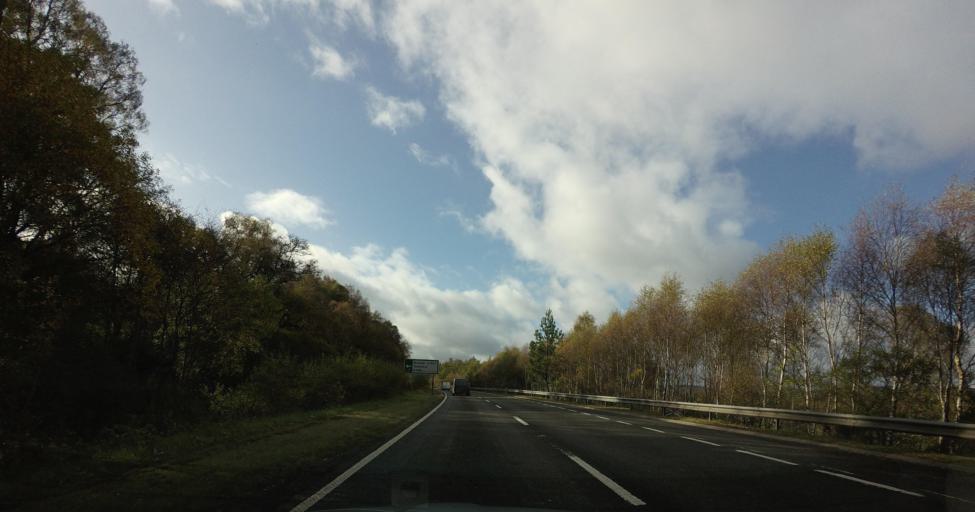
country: GB
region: Scotland
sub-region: Highland
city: Grantown on Spey
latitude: 57.3180
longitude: -3.5876
